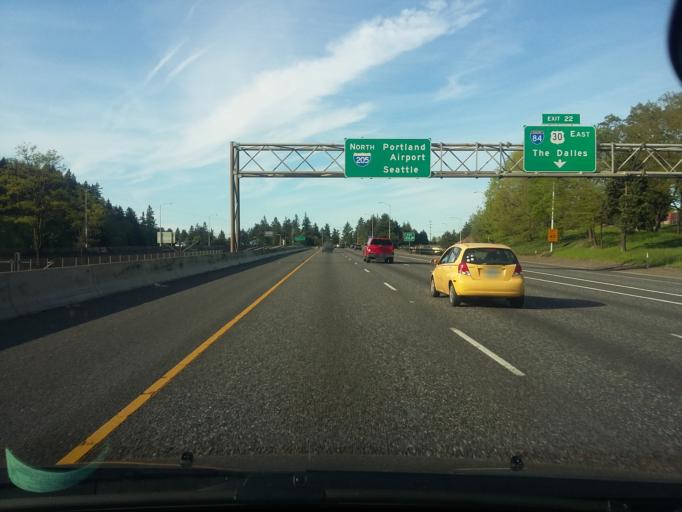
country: US
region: Oregon
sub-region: Multnomah County
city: Lents
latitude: 45.5429
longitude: -122.5616
